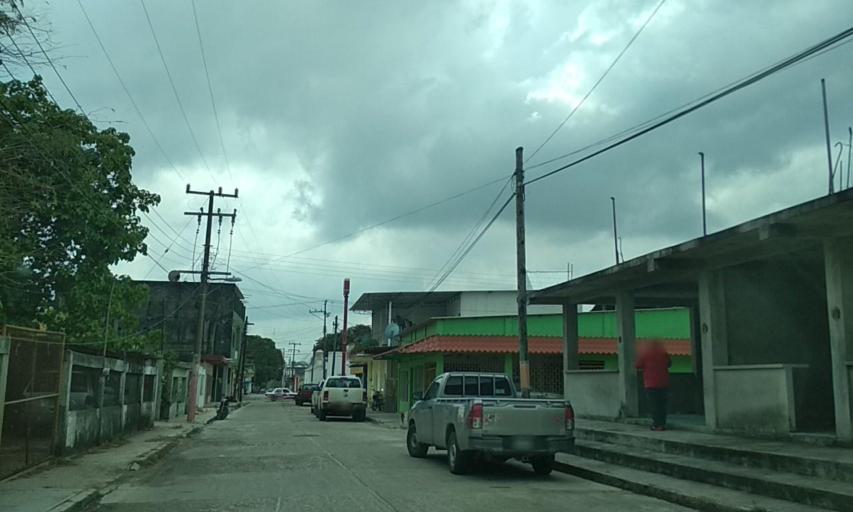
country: MX
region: Veracruz
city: Las Choapas
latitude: 17.8982
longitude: -94.1016
